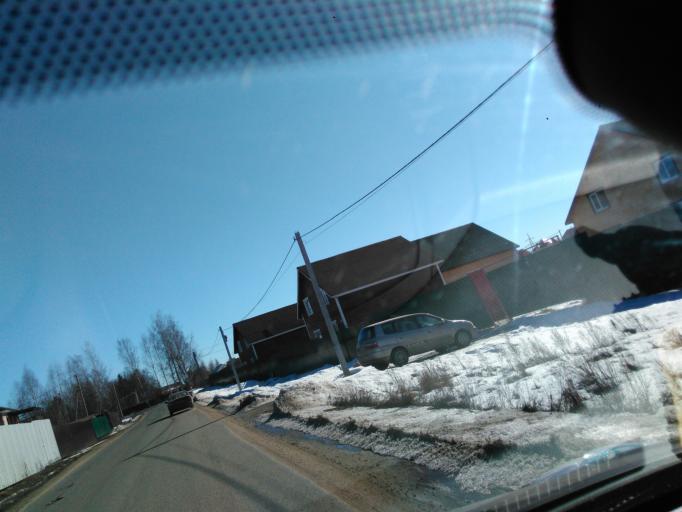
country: RU
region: Moskovskaya
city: Yermolino
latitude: 56.1523
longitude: 37.4827
